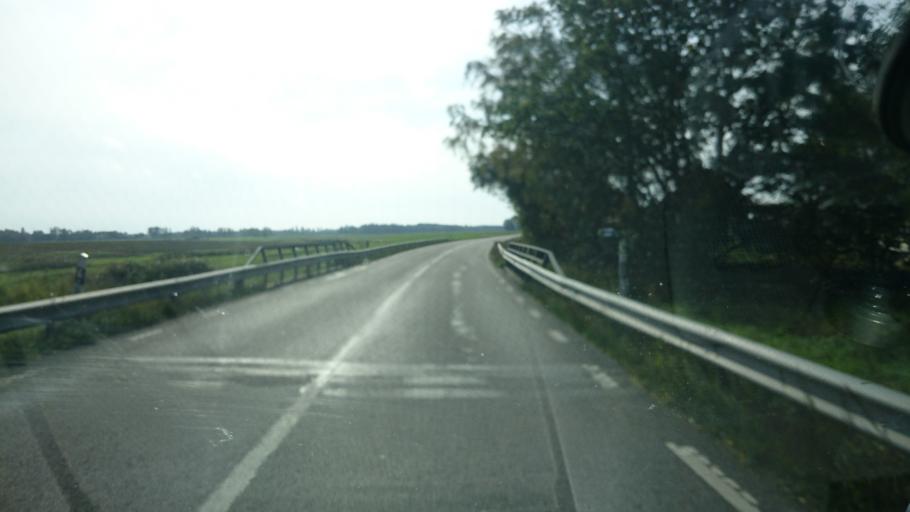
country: SE
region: Vaestra Goetaland
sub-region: Vanersborgs Kommun
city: Vargon
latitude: 58.2876
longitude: 12.3944
